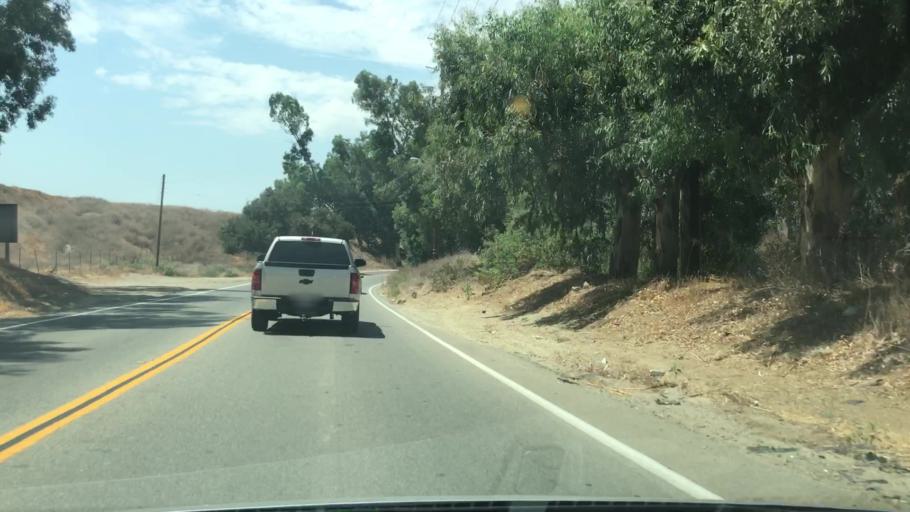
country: US
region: California
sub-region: Riverside County
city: Lake Elsinore
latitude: 33.7192
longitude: -117.3891
